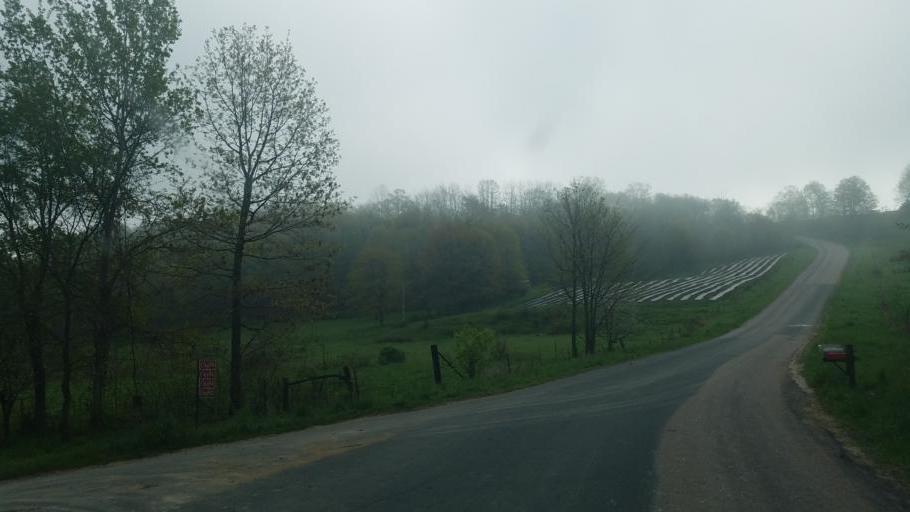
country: US
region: Wisconsin
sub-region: Vernon County
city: Hillsboro
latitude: 43.6277
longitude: -90.4222
